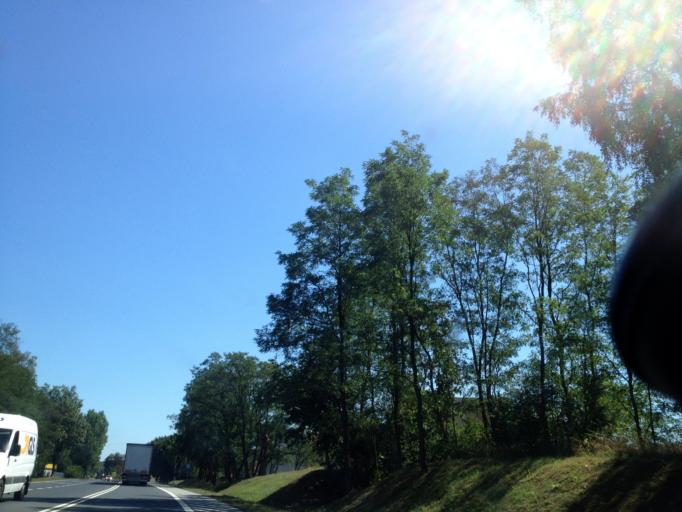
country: PL
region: Lubusz
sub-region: Powiat sulecinski
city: Torzym
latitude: 52.3153
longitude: 15.0526
